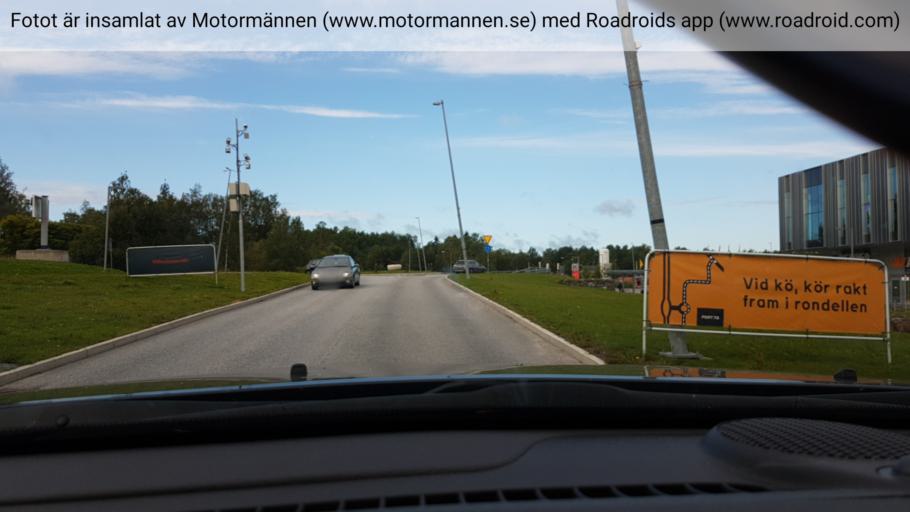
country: SE
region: Stockholm
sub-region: Haninge Kommun
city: Haninge
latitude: 59.1782
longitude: 18.1491
